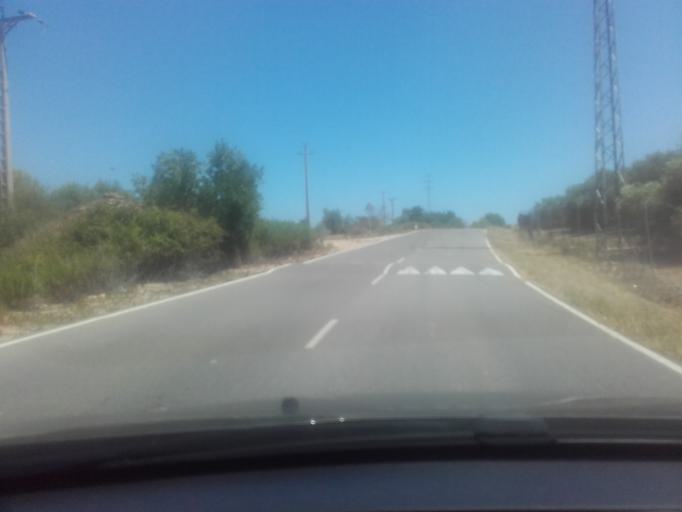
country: ES
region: Catalonia
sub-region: Provincia de Tarragona
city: Santa Oliva
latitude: 41.2682
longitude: 1.5348
